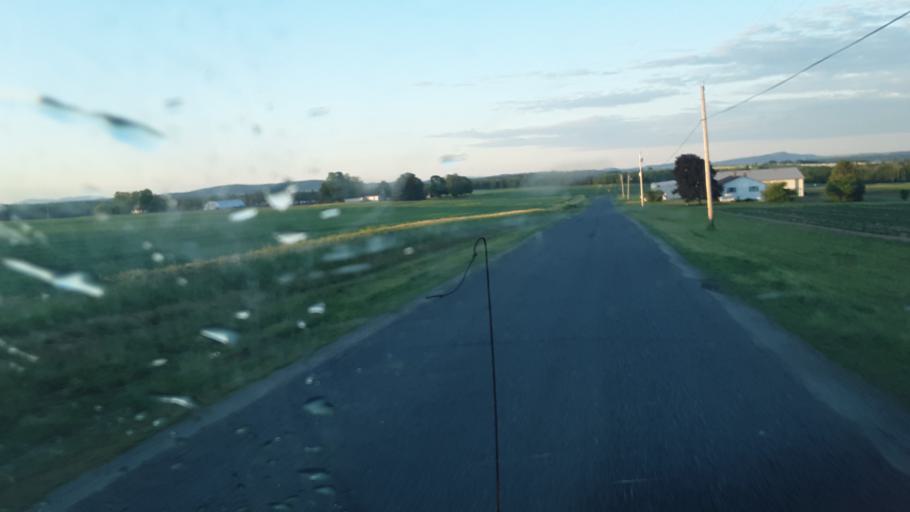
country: US
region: Maine
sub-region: Aroostook County
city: Caribou
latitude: 46.8061
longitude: -68.1350
